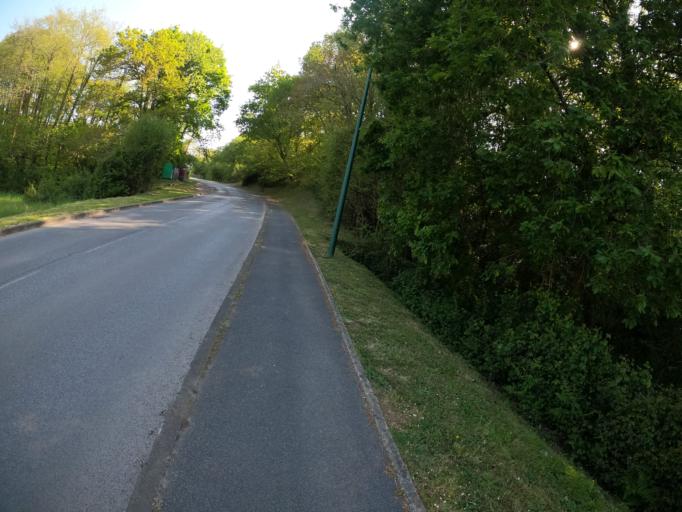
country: FR
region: Aquitaine
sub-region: Departement des Pyrenees-Atlantiques
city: Bassussarry
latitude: 43.4404
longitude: -1.5058
